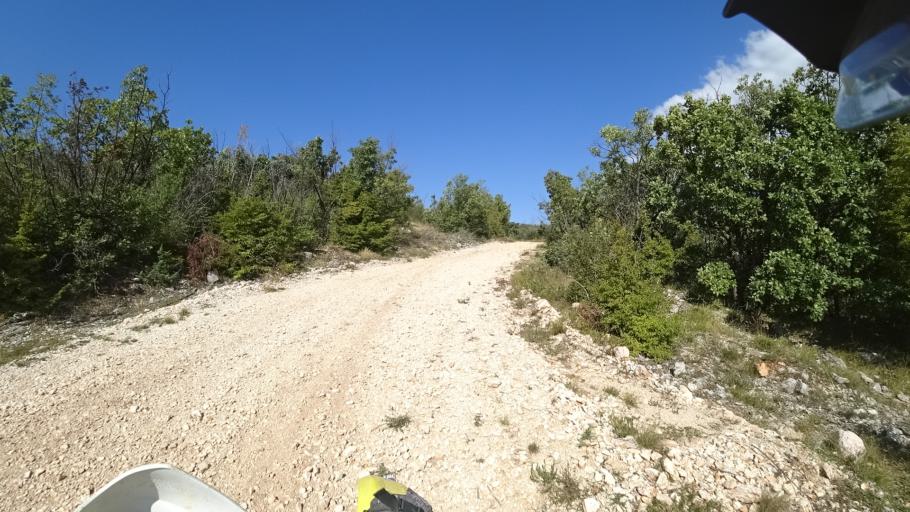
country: HR
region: Sibensko-Kniniska
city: Knin
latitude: 43.9586
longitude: 16.1609
